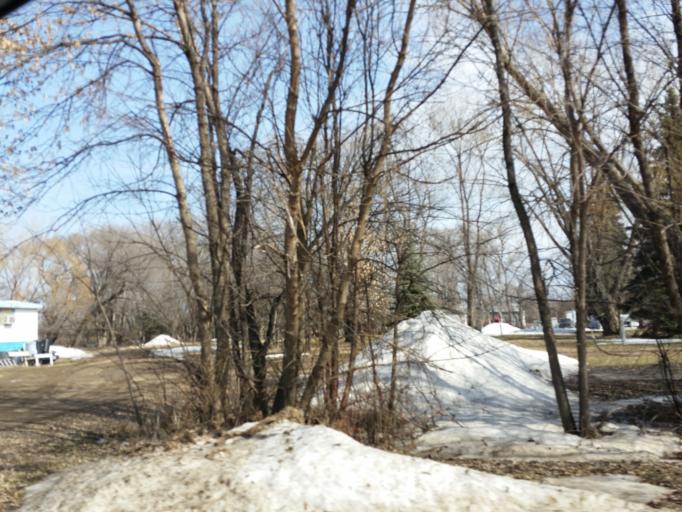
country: US
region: North Dakota
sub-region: Walsh County
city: Grafton
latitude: 48.4263
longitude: -97.4080
